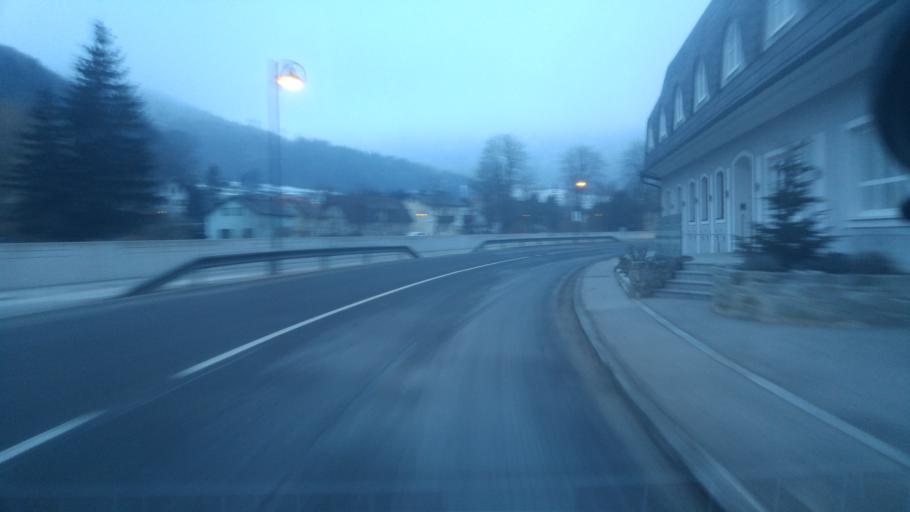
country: AT
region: Lower Austria
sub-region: Politischer Bezirk Baden
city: Weissenbach an der Triesting
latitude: 47.9833
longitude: 16.0369
